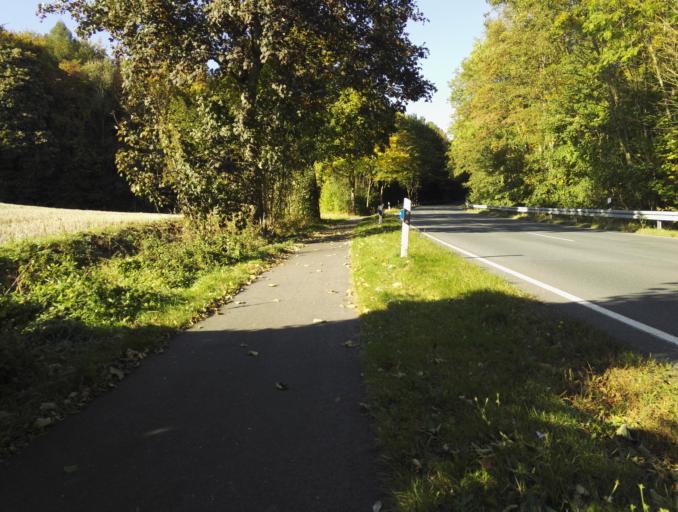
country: DE
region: Lower Saxony
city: Schellerten
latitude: 52.1229
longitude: 10.0938
